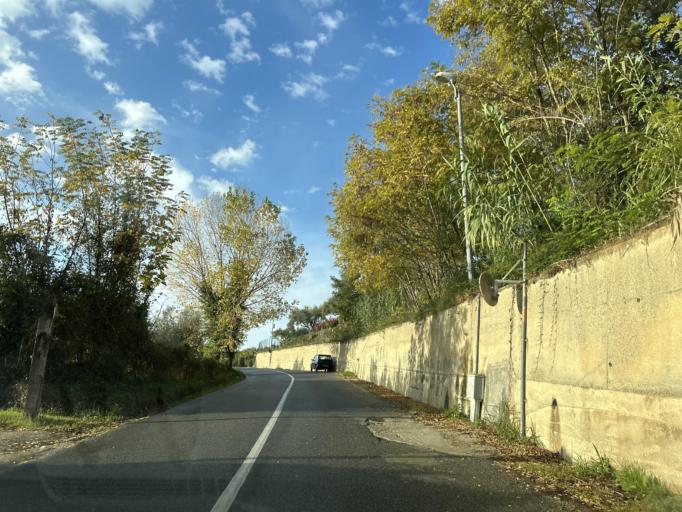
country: IT
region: Calabria
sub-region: Provincia di Catanzaro
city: Staletti
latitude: 38.7663
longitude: 16.5225
